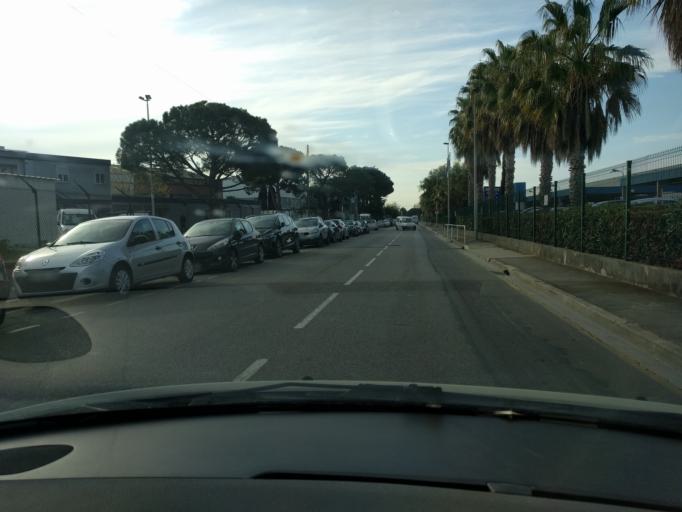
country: FR
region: Provence-Alpes-Cote d'Azur
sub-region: Departement des Alpes-Maritimes
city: Mandelieu-la-Napoule
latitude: 43.5484
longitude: 6.9655
